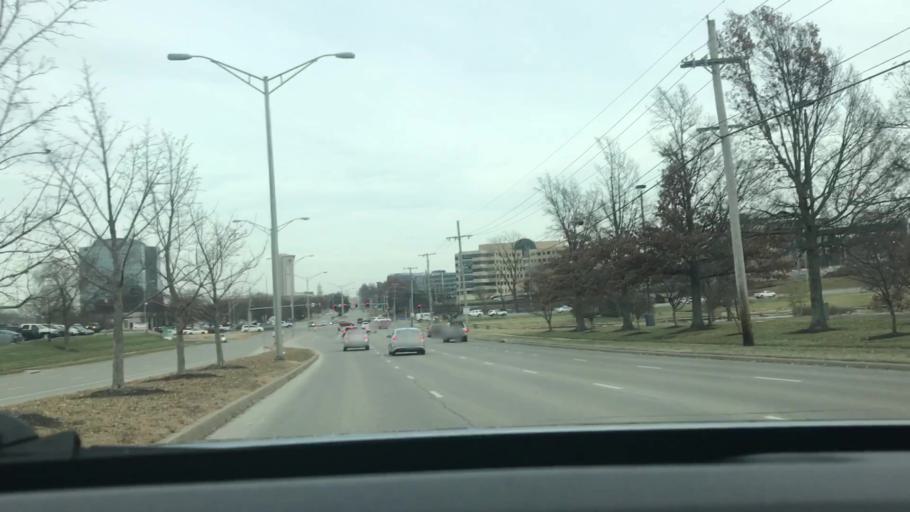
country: US
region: Kansas
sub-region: Johnson County
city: Overland Park
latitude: 38.9295
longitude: -94.6698
